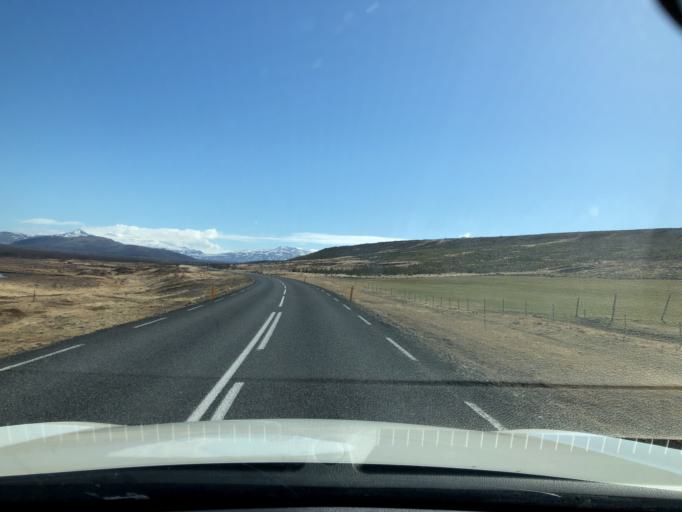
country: IS
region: South
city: Hveragerdi
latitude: 64.7001
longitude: -21.0378
